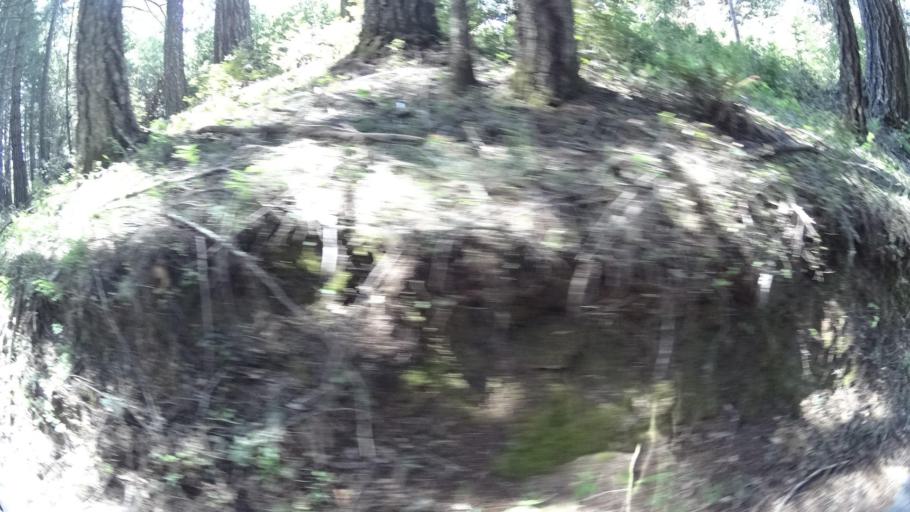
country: US
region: California
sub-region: Humboldt County
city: Redway
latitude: 40.0334
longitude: -123.6389
